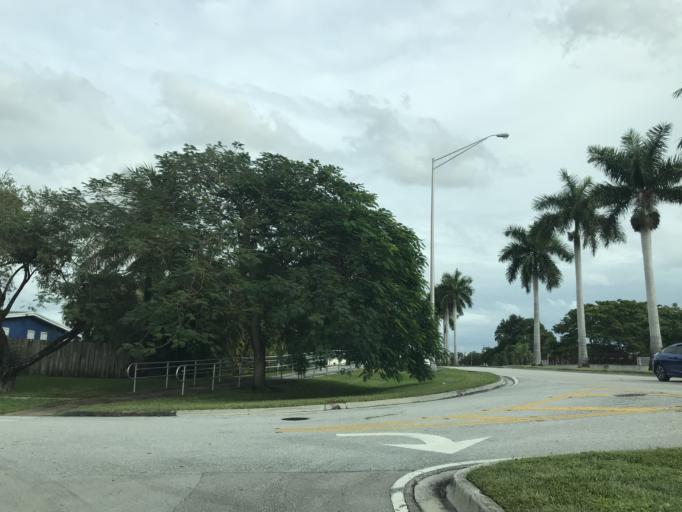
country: US
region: Florida
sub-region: Broward County
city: Margate
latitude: 26.2549
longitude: -80.2048
